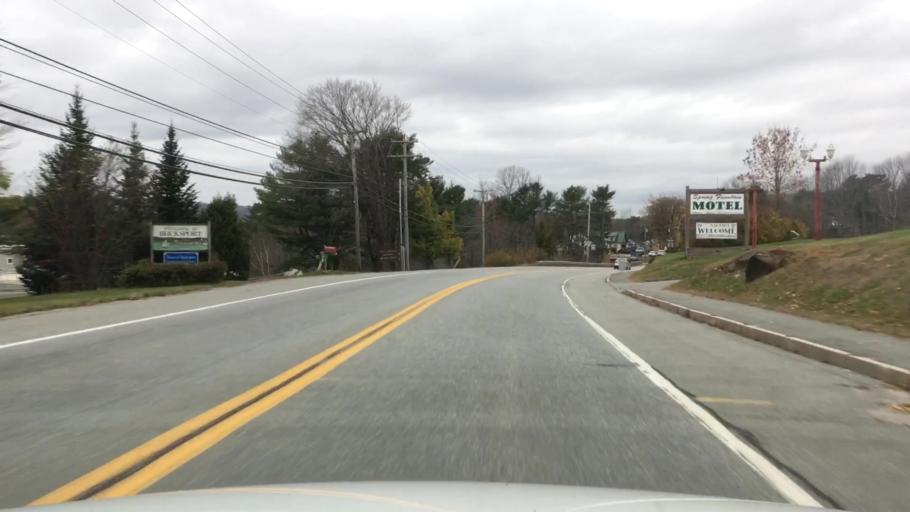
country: US
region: Maine
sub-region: Hancock County
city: Bucksport
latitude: 44.5694
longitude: -68.7714
